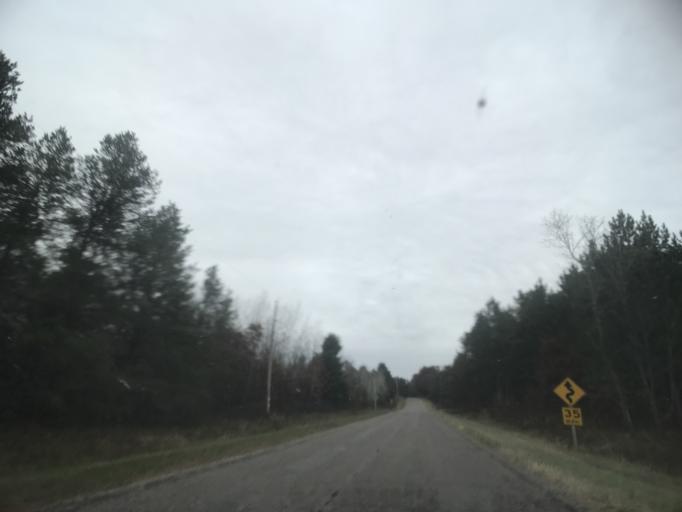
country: US
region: Wisconsin
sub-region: Oconto County
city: Gillett
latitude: 45.2741
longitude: -88.2571
